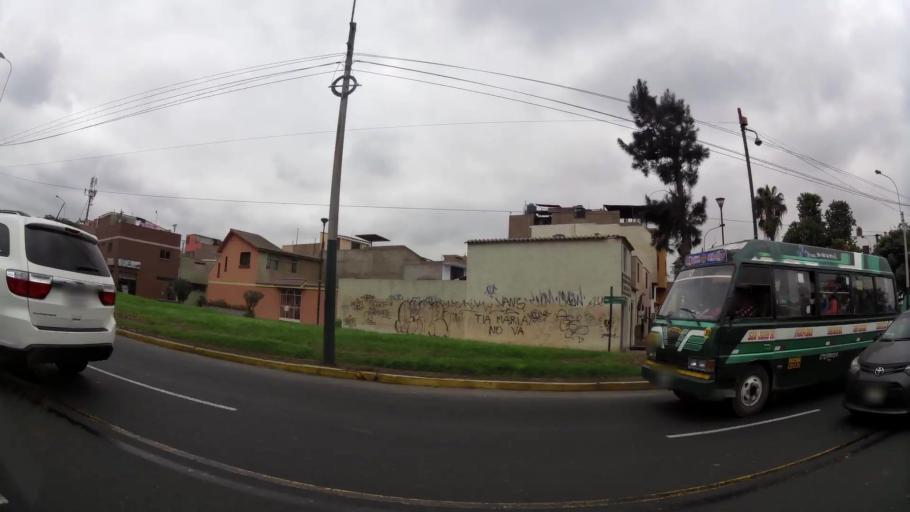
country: PE
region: Lima
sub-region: Lima
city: Surco
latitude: -12.1548
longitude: -76.9906
